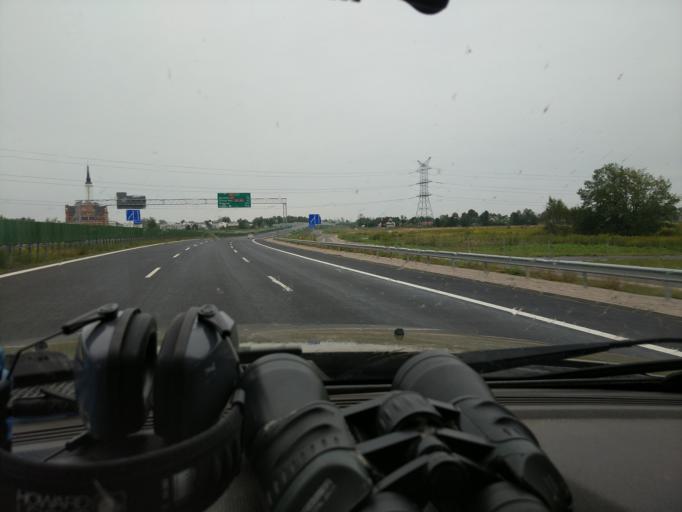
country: PL
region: Masovian Voivodeship
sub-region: Powiat wolominski
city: Radzymin
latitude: 52.4054
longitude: 21.2031
